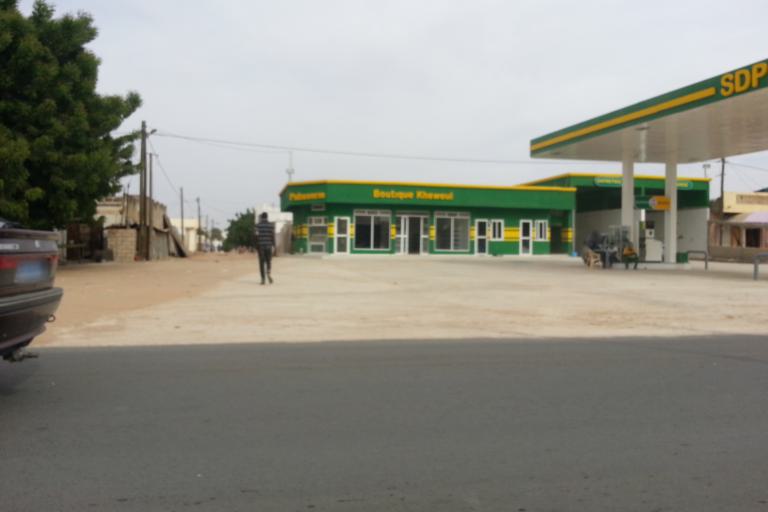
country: SN
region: Diourbel
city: Touba
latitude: 14.8507
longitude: -15.8921
